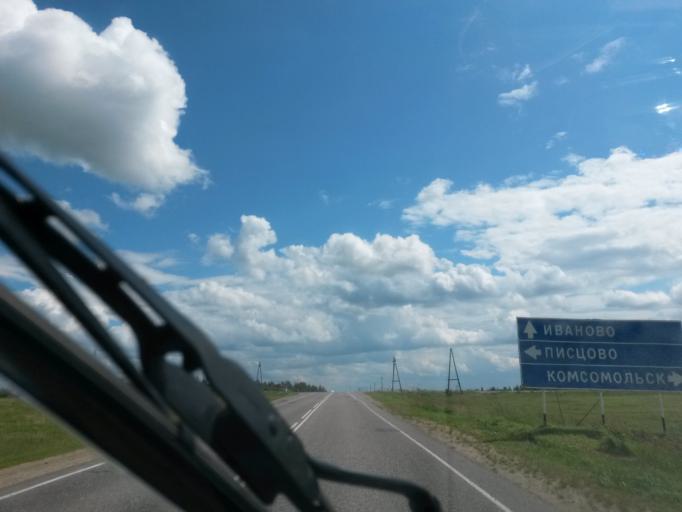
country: RU
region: Ivanovo
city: Pistsovo
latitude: 57.1755
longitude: 40.5002
